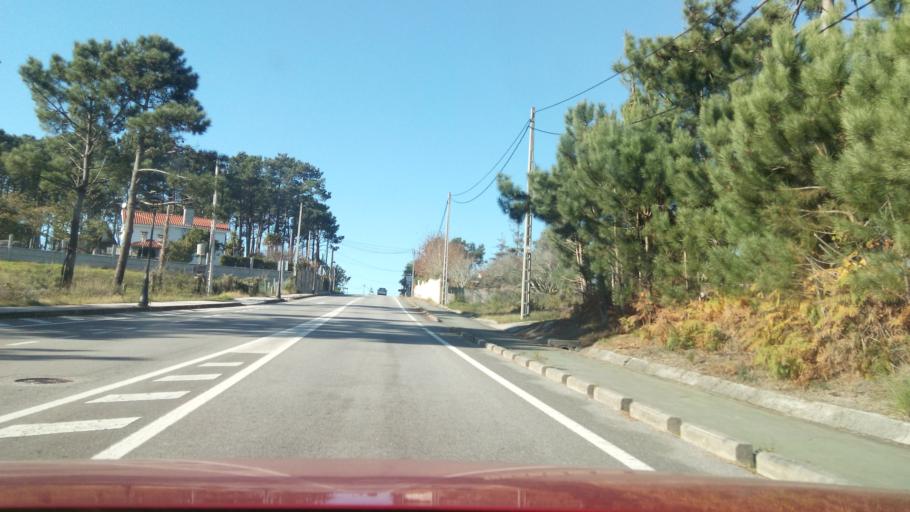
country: ES
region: Galicia
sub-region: Provincia de Pontevedra
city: O Grove
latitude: 42.4633
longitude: -8.9005
